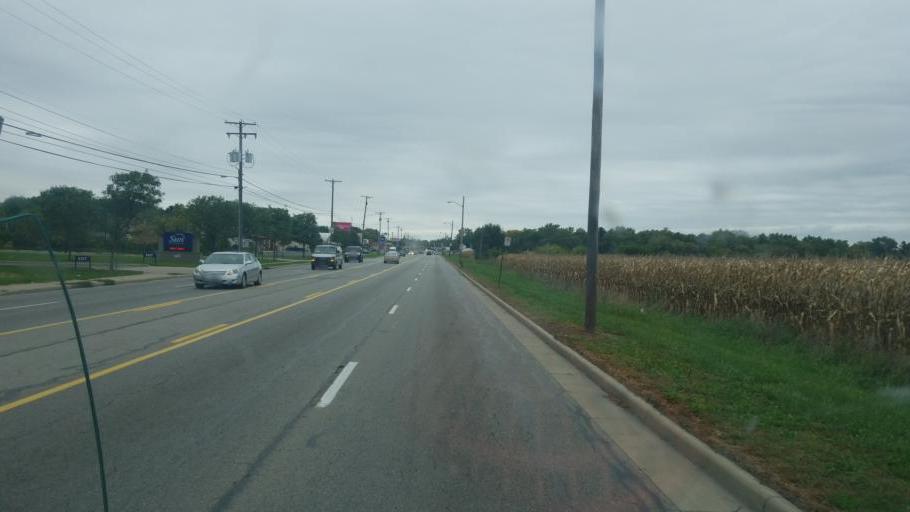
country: US
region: Ohio
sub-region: Lucas County
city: Ottawa Hills
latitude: 41.6420
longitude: -83.6645
